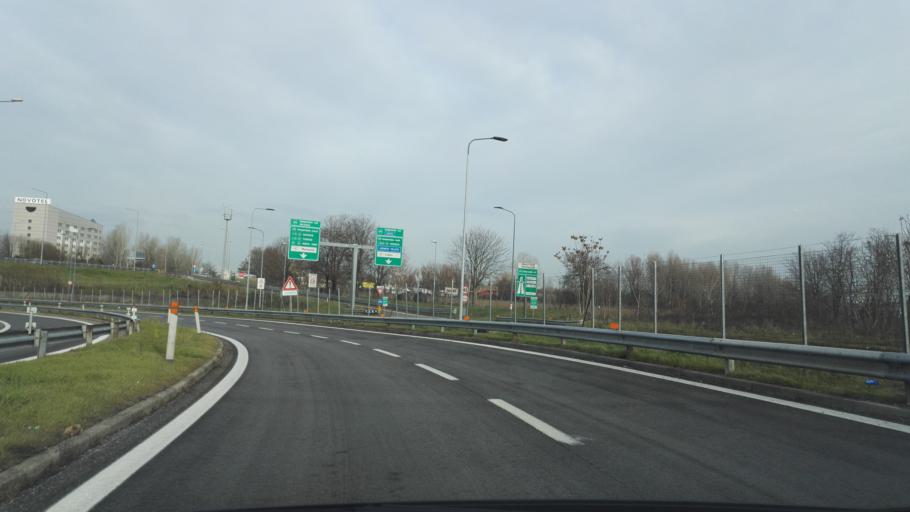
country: IT
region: Lombardy
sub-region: Citta metropolitana di Milano
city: Linate
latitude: 45.4451
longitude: 9.2602
